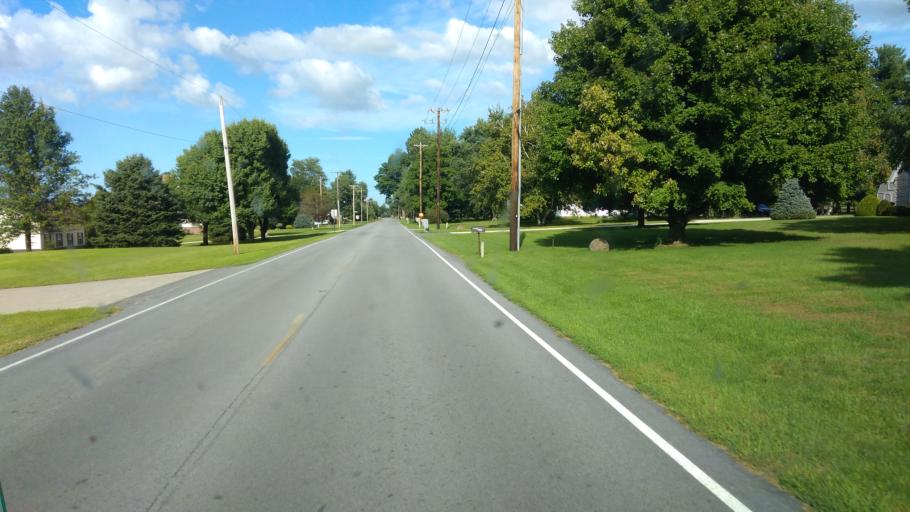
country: US
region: Ohio
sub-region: Sandusky County
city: Clyde
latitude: 41.2898
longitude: -82.9573
